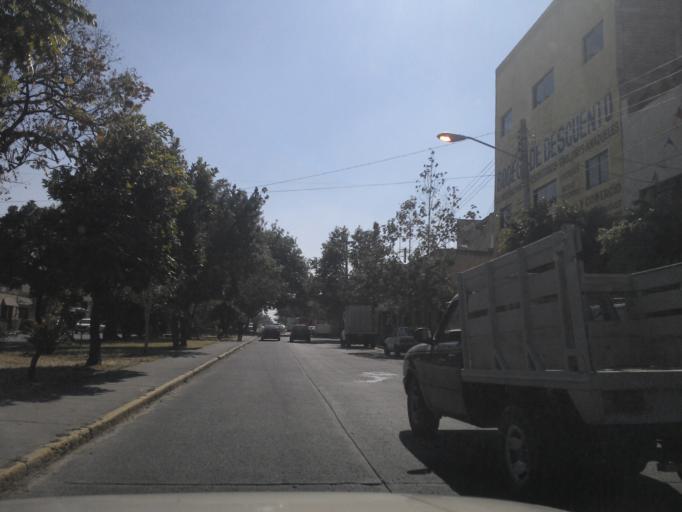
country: MX
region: Jalisco
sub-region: Zapopan
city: Zapopan
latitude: 20.7006
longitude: -103.3578
